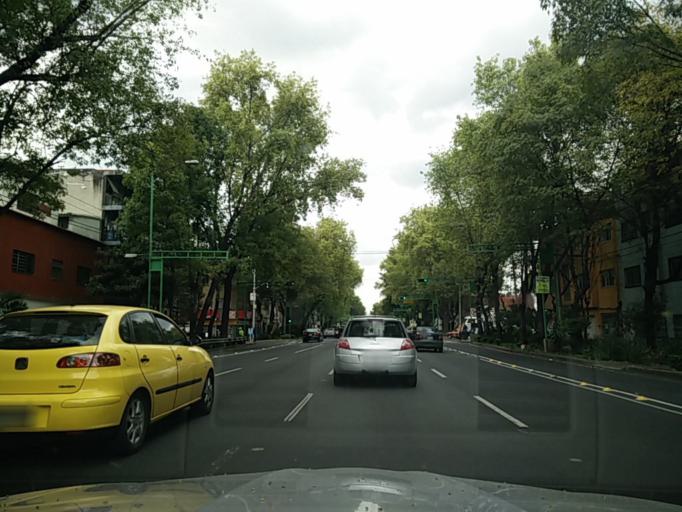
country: MX
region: Mexico City
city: Benito Juarez
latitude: 19.3990
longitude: -99.1455
